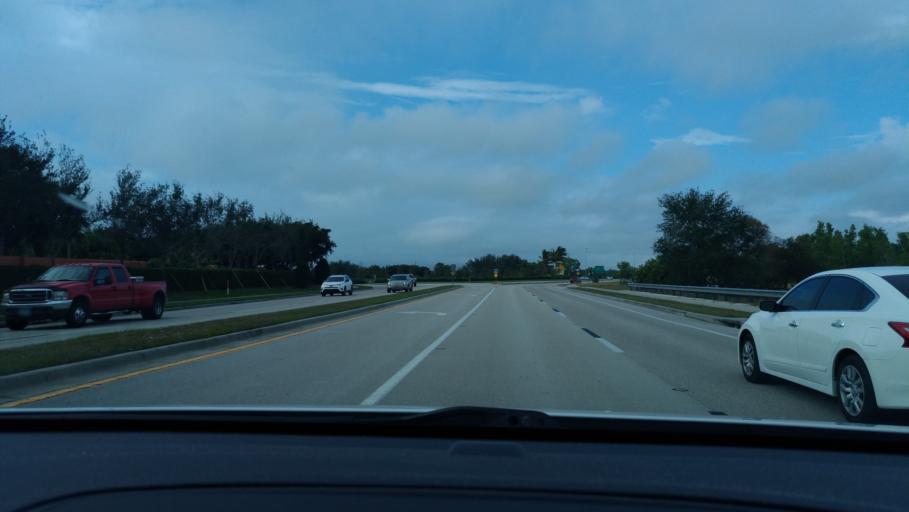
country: US
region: Florida
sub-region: Lee County
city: Estero
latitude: 26.4178
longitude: -81.8057
